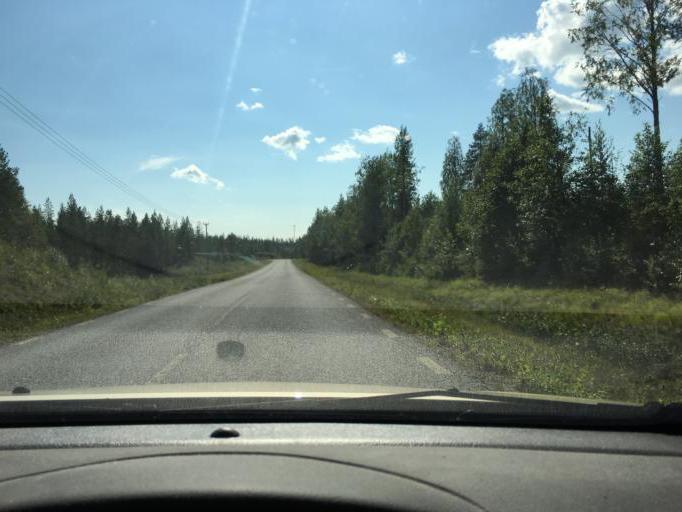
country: SE
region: Norrbotten
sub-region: Kalix Kommun
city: Toere
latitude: 66.0584
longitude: 22.5987
